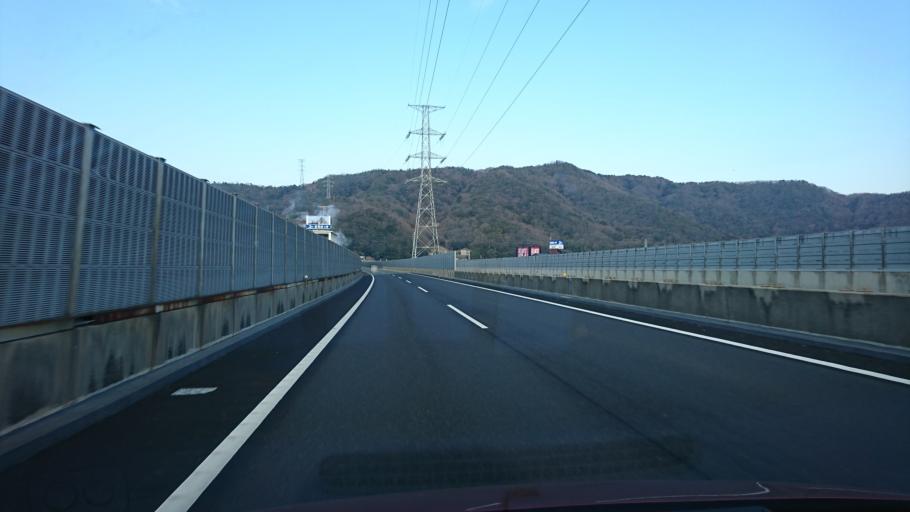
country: JP
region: Hyogo
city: Himeji
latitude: 34.8581
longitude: 134.7247
